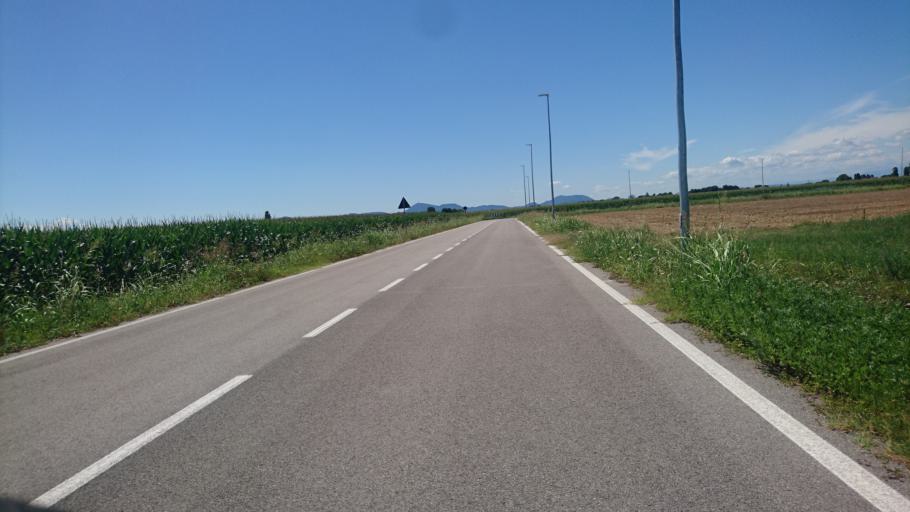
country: IT
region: Veneto
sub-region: Provincia di Padova
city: Ponte San Nicolo
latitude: 45.3419
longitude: 11.9294
